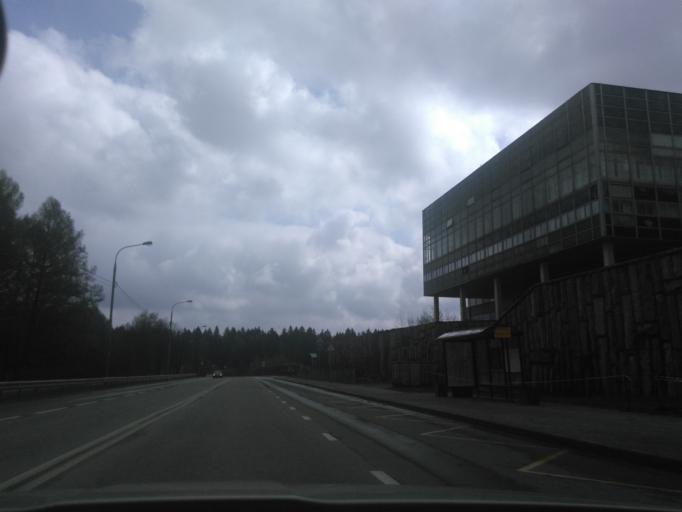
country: RU
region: Moskovskaya
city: Rzhavki
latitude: 55.9845
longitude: 37.2203
